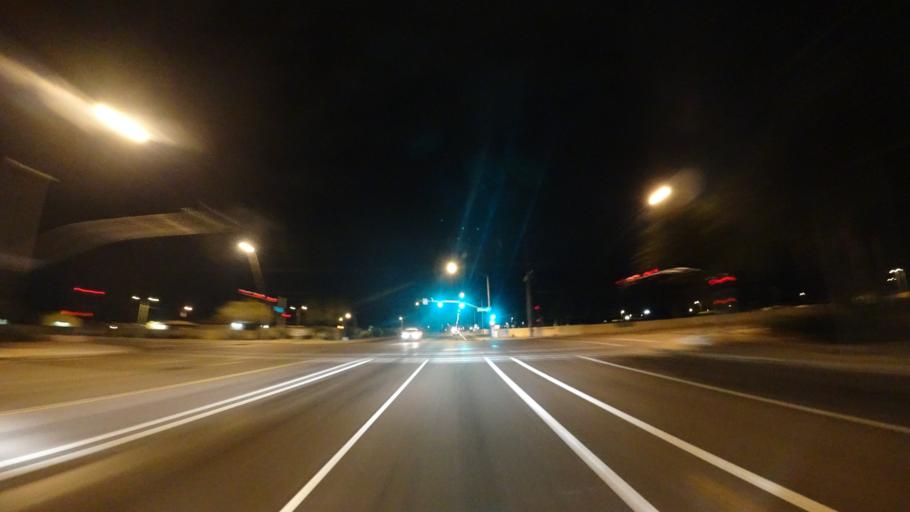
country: US
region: Arizona
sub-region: Maricopa County
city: Gilbert
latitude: 33.4079
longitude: -111.7191
